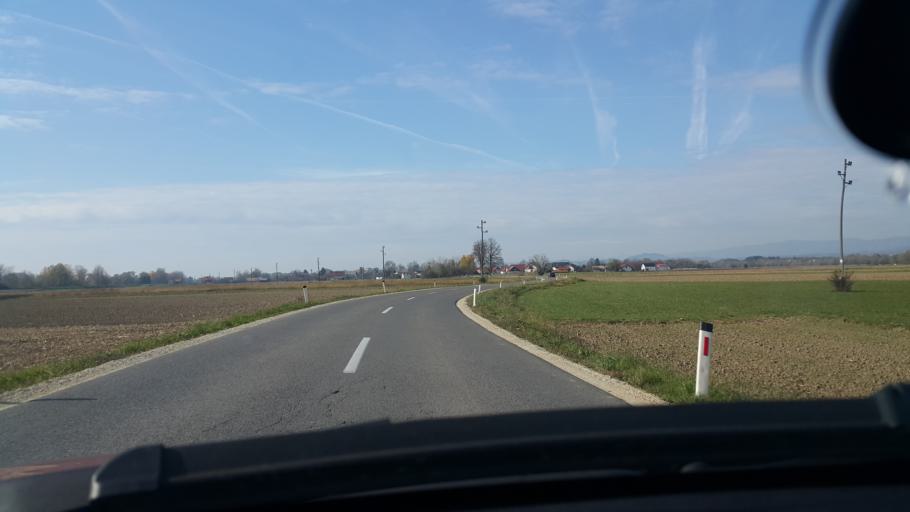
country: SI
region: Brezice
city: Brezice
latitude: 45.8960
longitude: 15.6399
